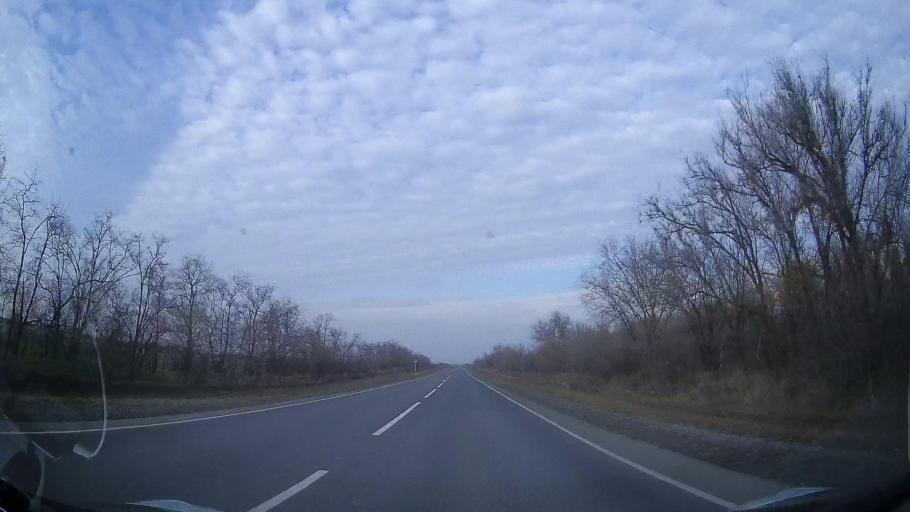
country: RU
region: Rostov
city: Bagayevskaya
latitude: 47.1455
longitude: 40.2766
